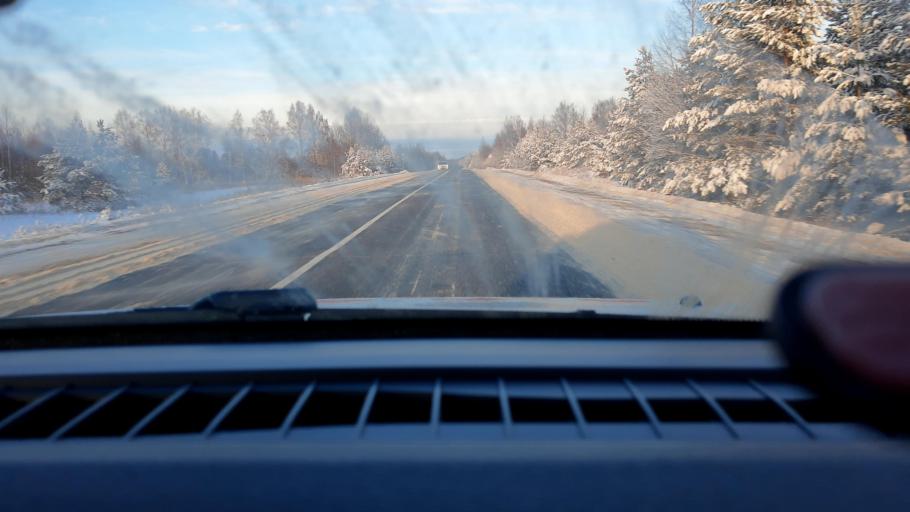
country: RU
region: Nizjnij Novgorod
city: Tonkino
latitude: 57.3158
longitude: 46.4701
